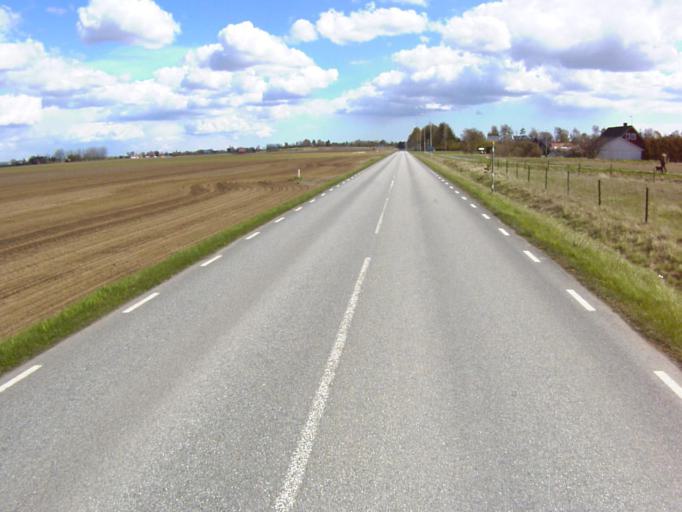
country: SE
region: Skane
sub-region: Kristianstads Kommun
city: Kristianstad
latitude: 56.0164
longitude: 14.0875
